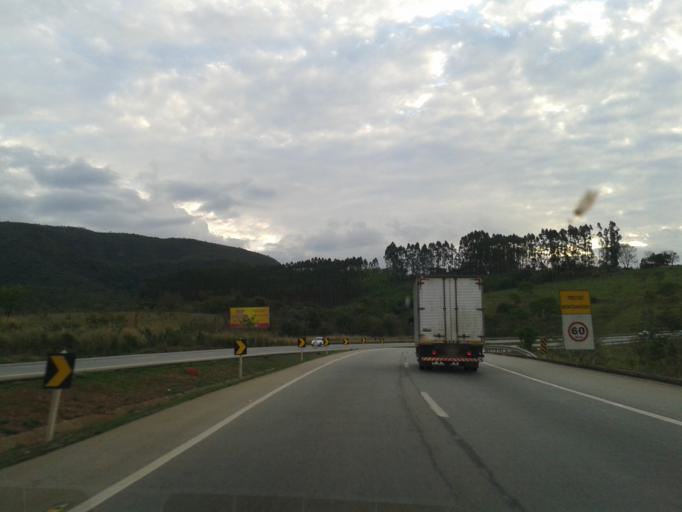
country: BR
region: Minas Gerais
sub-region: Mateus Leme
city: Mateus Leme
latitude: -19.9331
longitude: -44.4211
